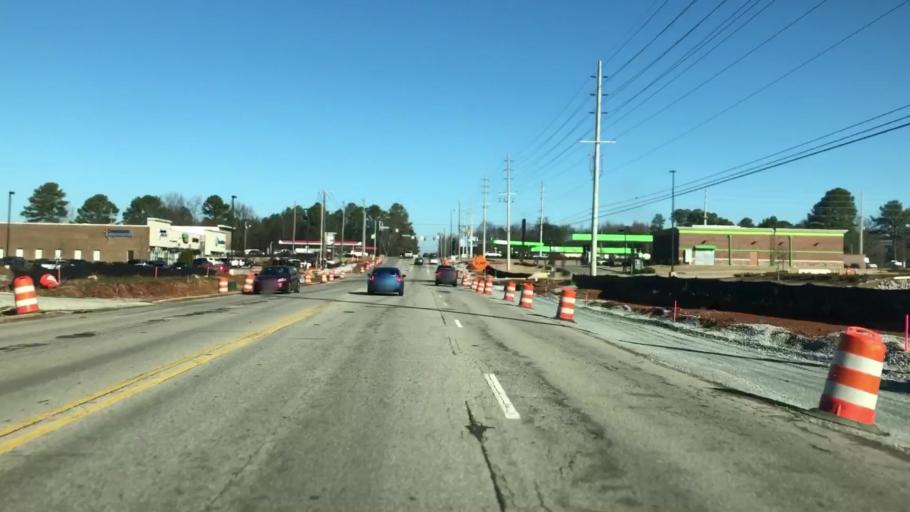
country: US
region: Alabama
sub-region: Madison County
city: Madison
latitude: 34.7457
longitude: -86.7861
